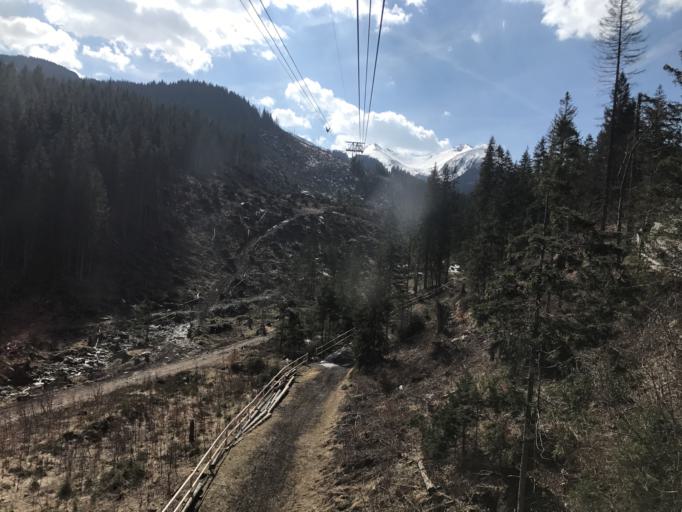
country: PL
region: Lesser Poland Voivodeship
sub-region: Powiat tatrzanski
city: Zakopane
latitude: 49.2674
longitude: 19.9785
